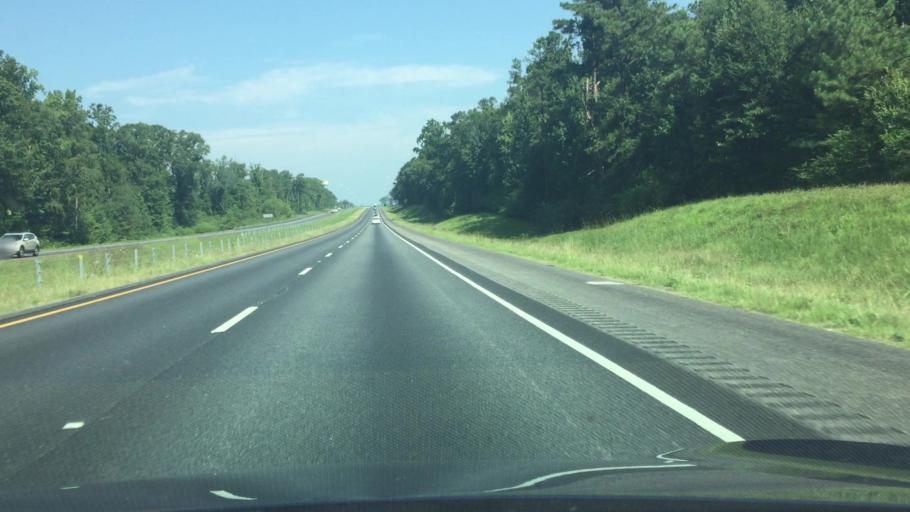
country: US
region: Alabama
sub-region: Chilton County
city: Thorsby
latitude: 32.9658
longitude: -86.6784
